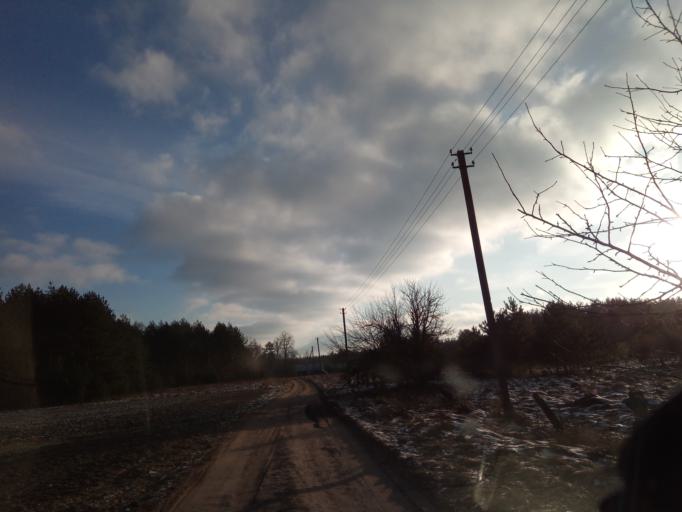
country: LT
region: Alytaus apskritis
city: Druskininkai
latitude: 53.9767
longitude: 24.2425
